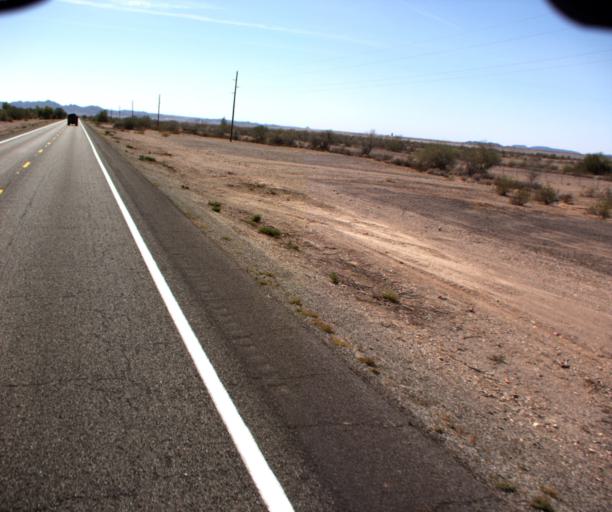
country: US
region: Arizona
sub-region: Yuma County
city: Fortuna Foothills
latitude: 32.8967
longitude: -114.3360
